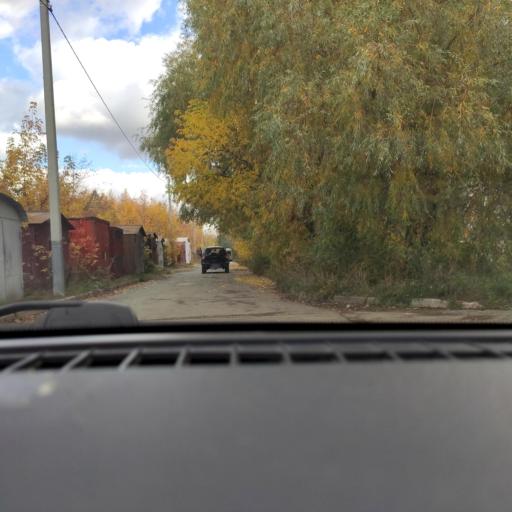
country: RU
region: Perm
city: Kondratovo
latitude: 58.0058
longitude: 56.1126
